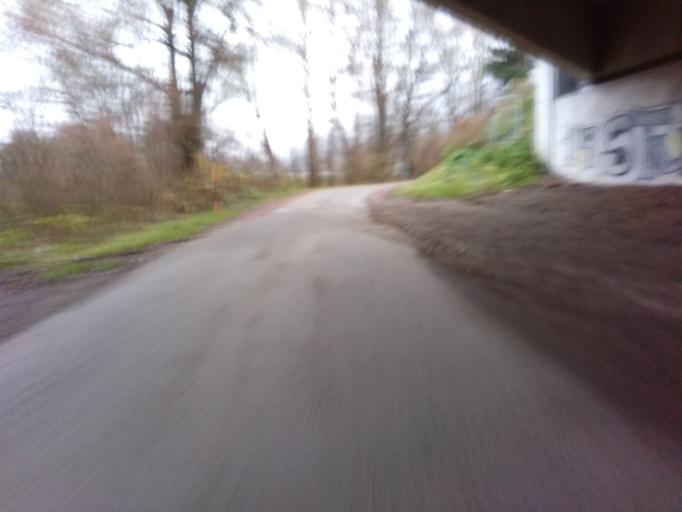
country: AT
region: Styria
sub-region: Politischer Bezirk Bruck-Muerzzuschlag
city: Frauenberg
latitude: 47.4496
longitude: 15.3254
